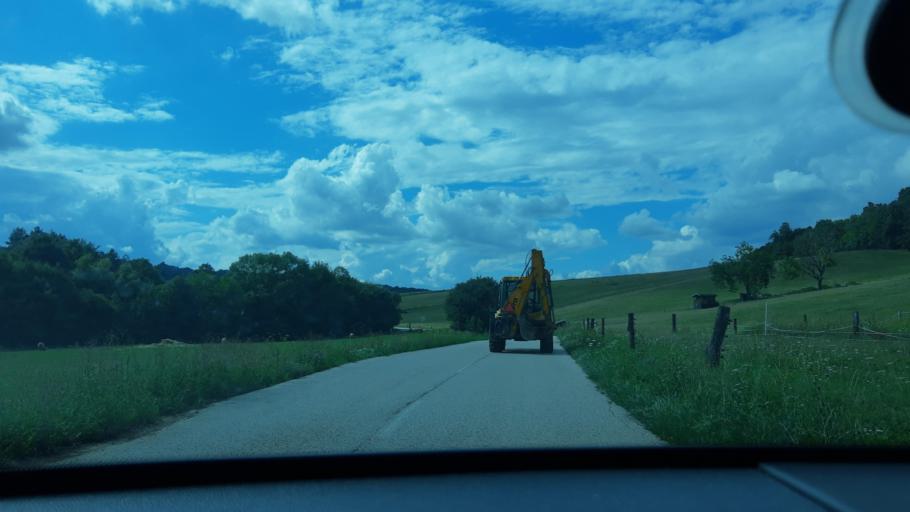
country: SK
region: Trnavsky
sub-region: Okres Trnava
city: Piestany
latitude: 48.6360
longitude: 17.9127
